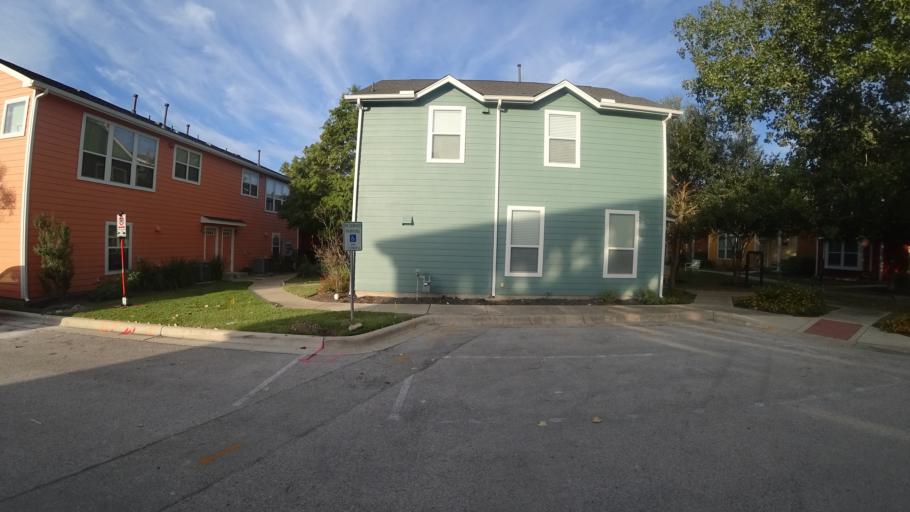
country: US
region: Texas
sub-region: Travis County
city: Austin
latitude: 30.2781
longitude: -97.7103
